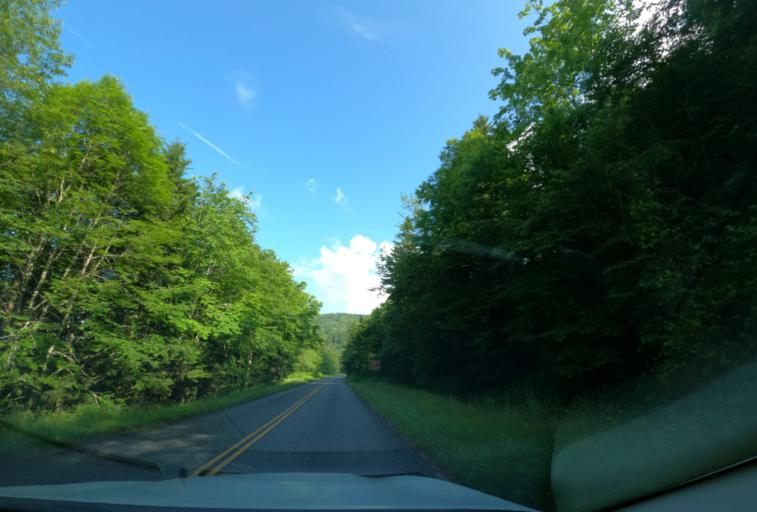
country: US
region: North Carolina
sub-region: Haywood County
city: Hazelwood
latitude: 35.3379
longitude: -82.9690
